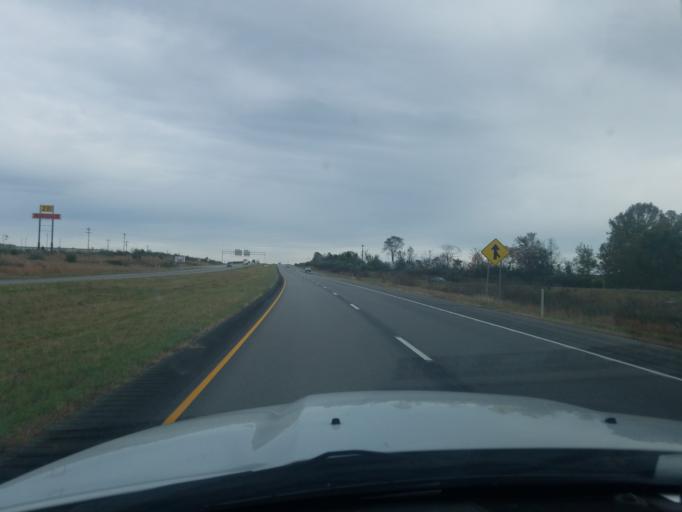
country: US
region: Indiana
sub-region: Spencer County
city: Dale
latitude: 38.1935
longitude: -86.9770
